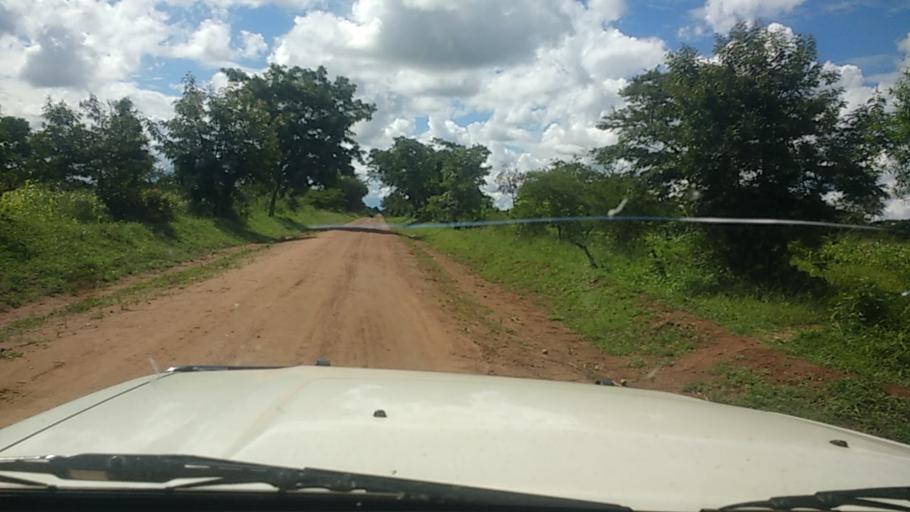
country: UG
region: Eastern Region
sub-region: Katakwi District
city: Katakwi
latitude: 1.7680
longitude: 33.9529
